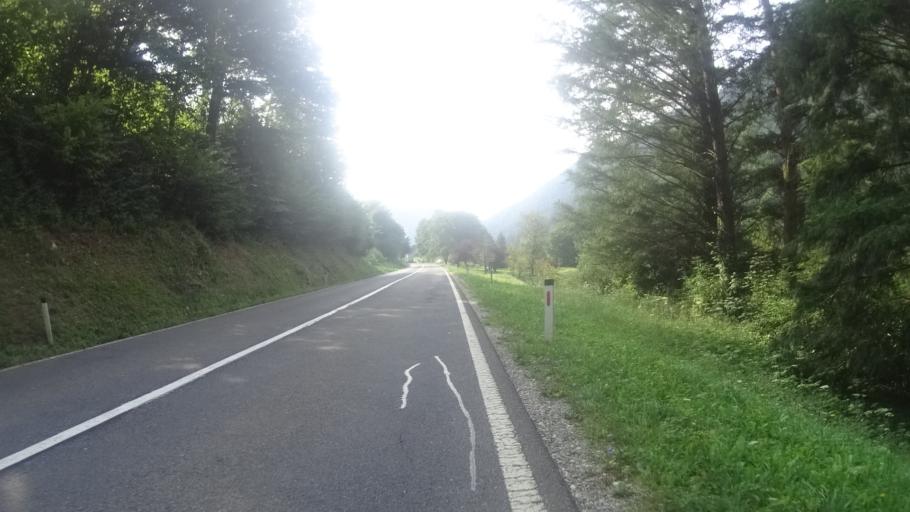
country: SI
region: Lovrenc na Pohorju
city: Lovrenc na Pohorju
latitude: 46.5774
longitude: 15.4070
